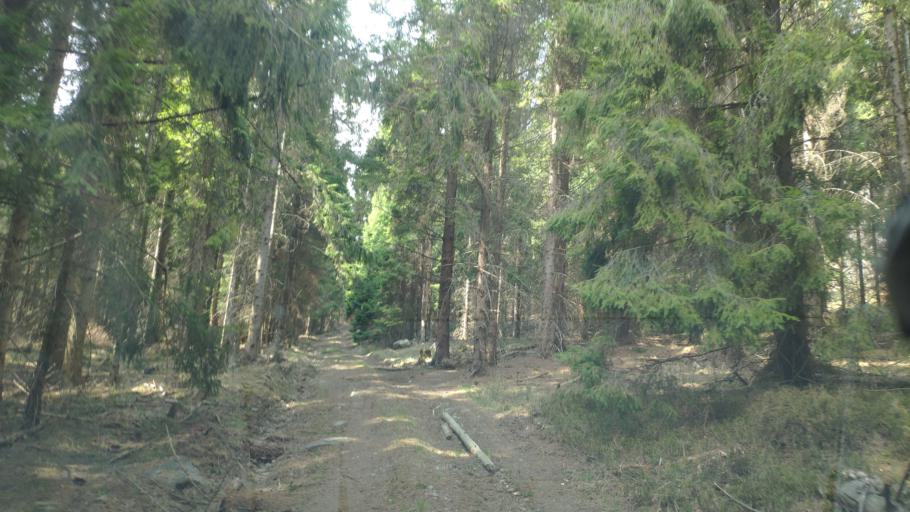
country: SK
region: Kosicky
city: Gelnica
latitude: 48.7582
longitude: 21.0194
